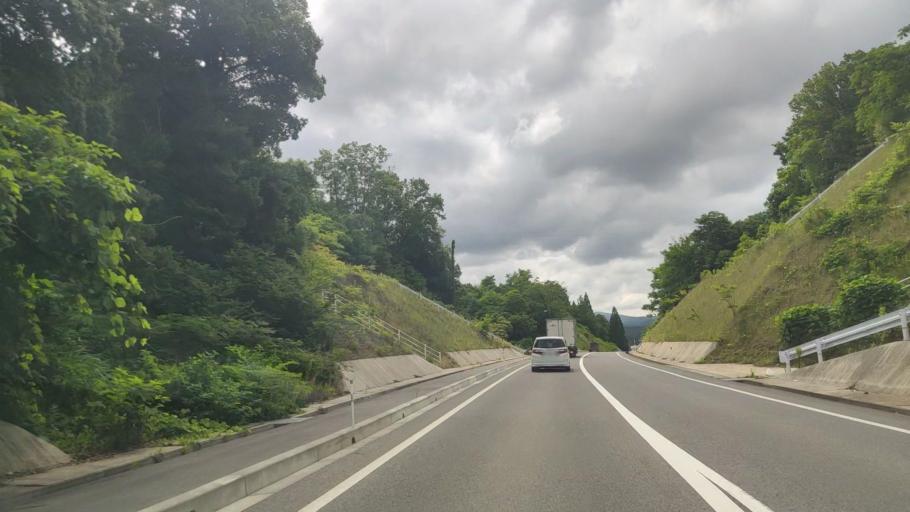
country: JP
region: Tottori
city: Yonago
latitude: 35.3763
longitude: 133.4057
